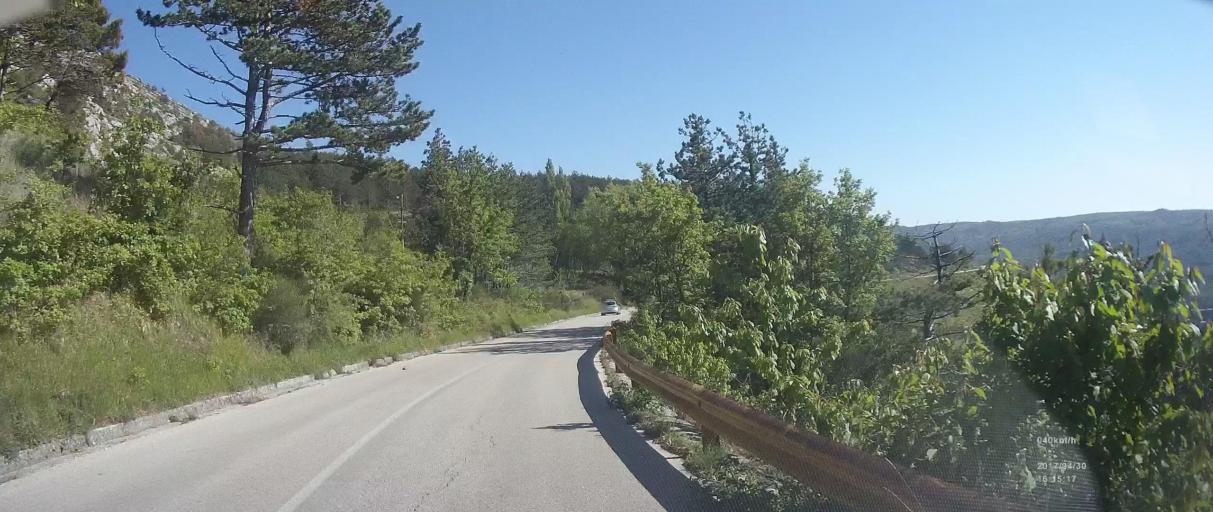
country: HR
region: Splitsko-Dalmatinska
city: Srinjine
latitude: 43.5090
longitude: 16.6061
